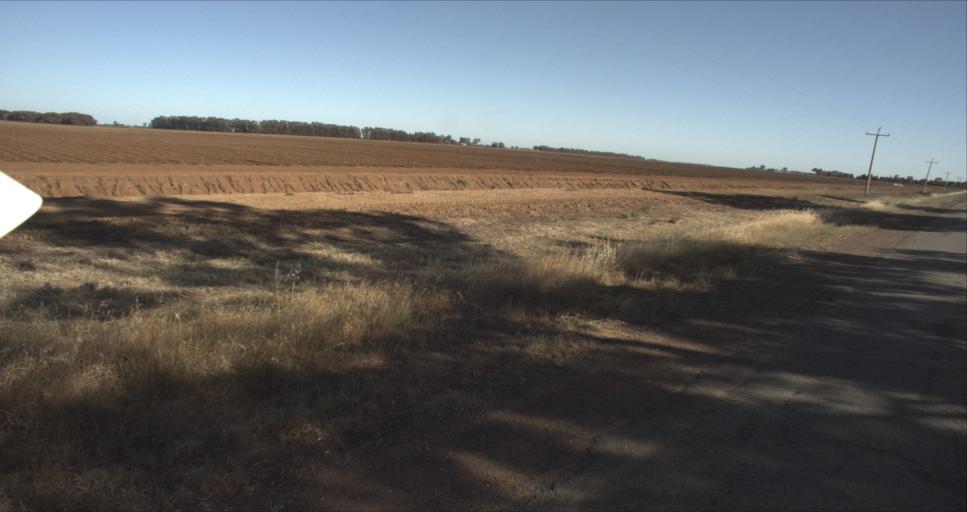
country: AU
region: New South Wales
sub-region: Leeton
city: Leeton
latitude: -34.5988
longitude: 146.2581
